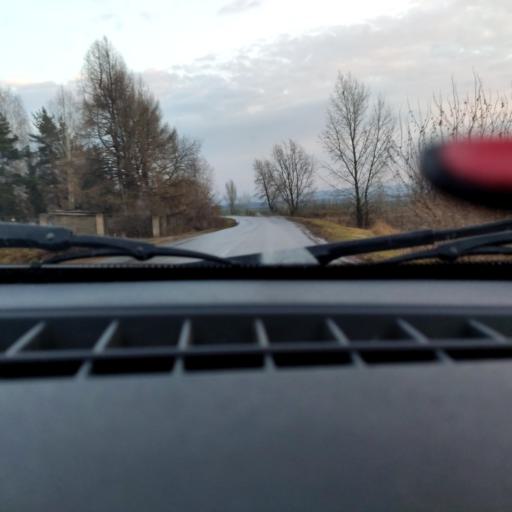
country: RU
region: Bashkortostan
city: Avdon
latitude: 54.5114
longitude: 55.8236
